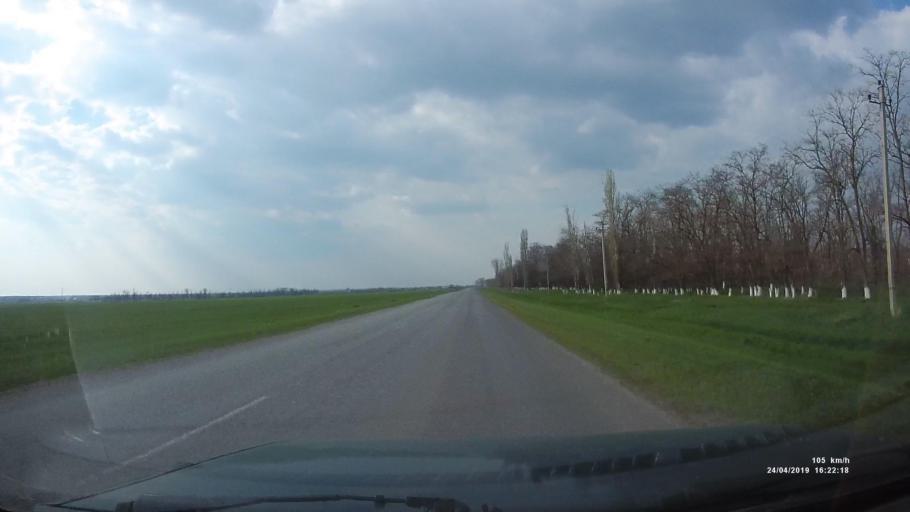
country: RU
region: Rostov
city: Orlovskiy
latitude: 46.8176
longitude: 42.0574
